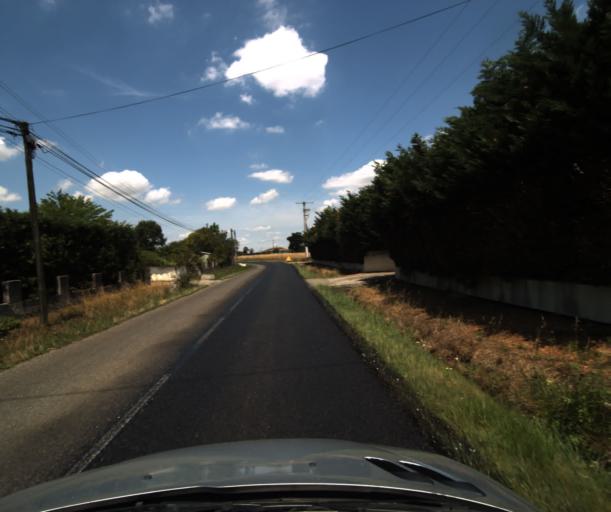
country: FR
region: Midi-Pyrenees
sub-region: Departement de la Haute-Garonne
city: Saint-Lys
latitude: 43.4979
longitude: 1.1989
